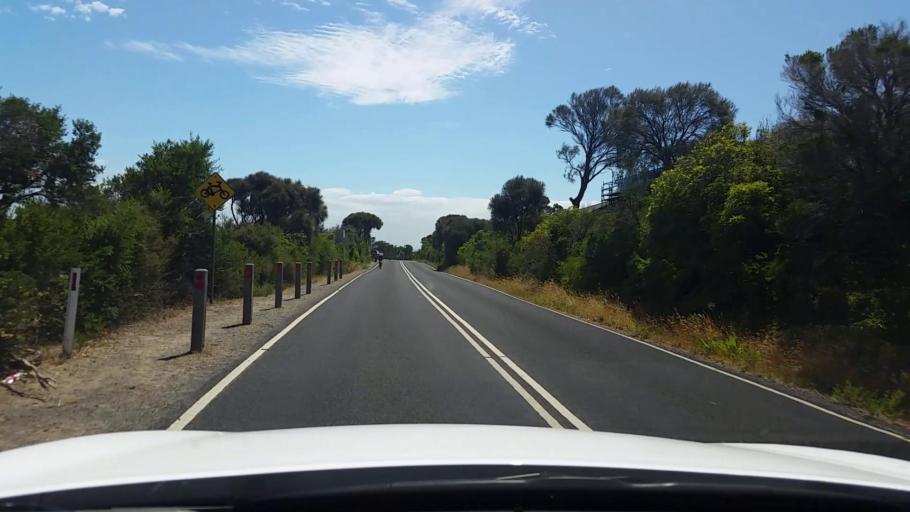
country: AU
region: Victoria
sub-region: Mornington Peninsula
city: Mount Martha
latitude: -38.2730
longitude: 145.0016
